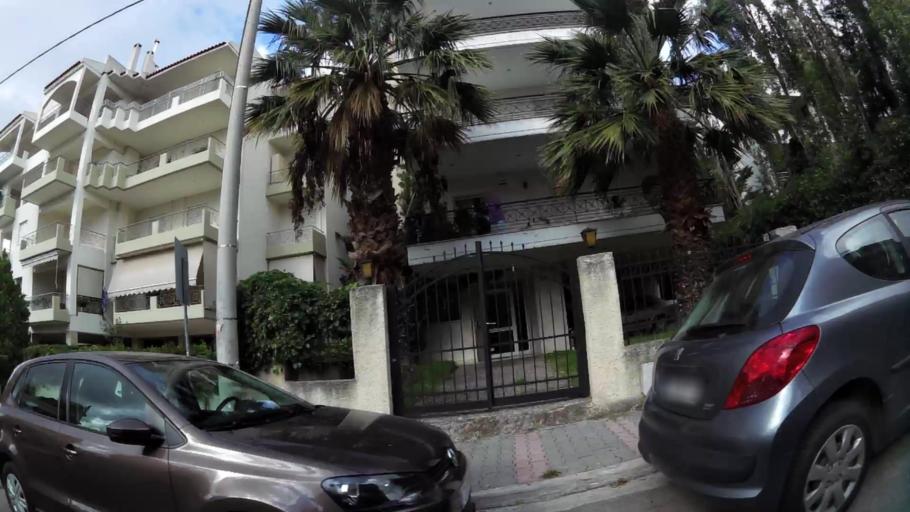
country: GR
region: Attica
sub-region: Nomarchia Athinas
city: Melissia
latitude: 38.0584
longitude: 23.8336
